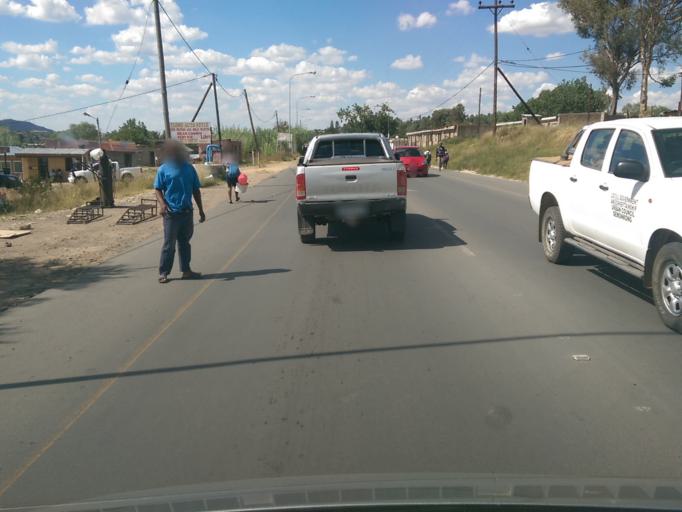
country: LS
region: Maseru
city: Maseru
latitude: -29.3103
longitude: 27.5126
